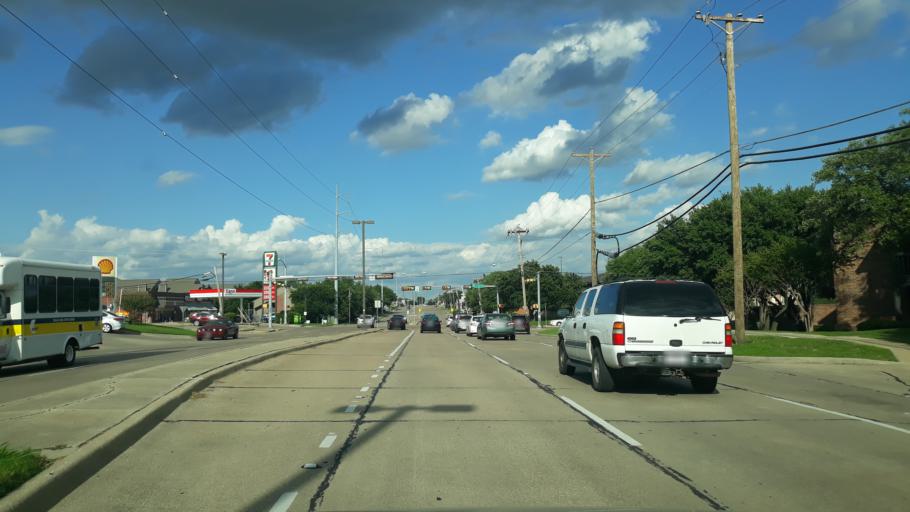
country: US
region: Texas
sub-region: Dallas County
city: Irving
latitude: 32.8570
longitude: -97.0090
